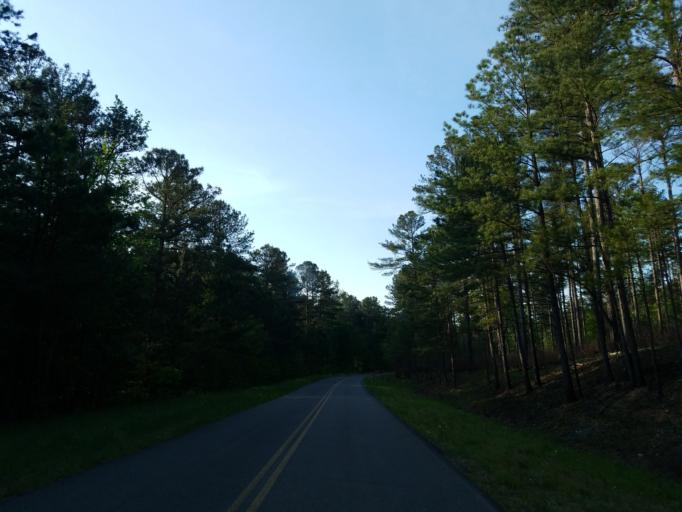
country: US
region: Georgia
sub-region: Gordon County
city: Calhoun
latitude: 34.6101
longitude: -85.0812
